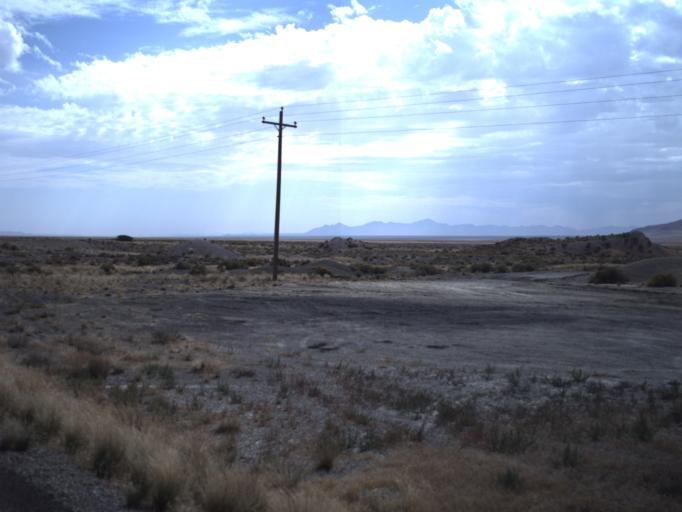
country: US
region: Utah
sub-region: Tooele County
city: Wendover
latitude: 41.4276
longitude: -113.8316
